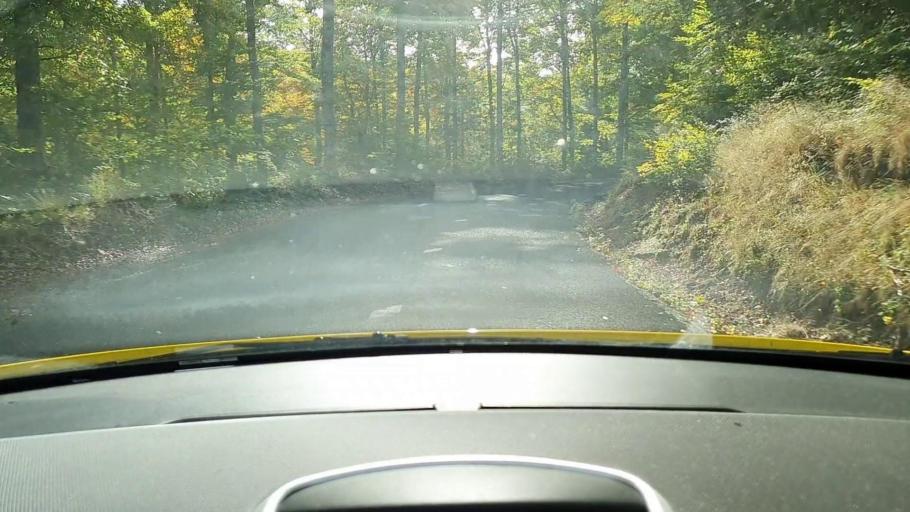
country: FR
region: Languedoc-Roussillon
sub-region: Departement du Gard
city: Valleraugue
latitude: 44.0711
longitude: 3.5686
